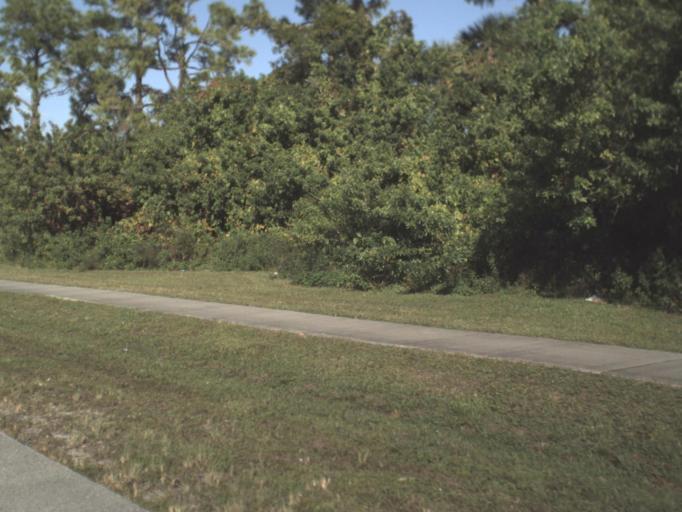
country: US
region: Florida
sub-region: Brevard County
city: June Park
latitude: 28.0058
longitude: -80.6720
